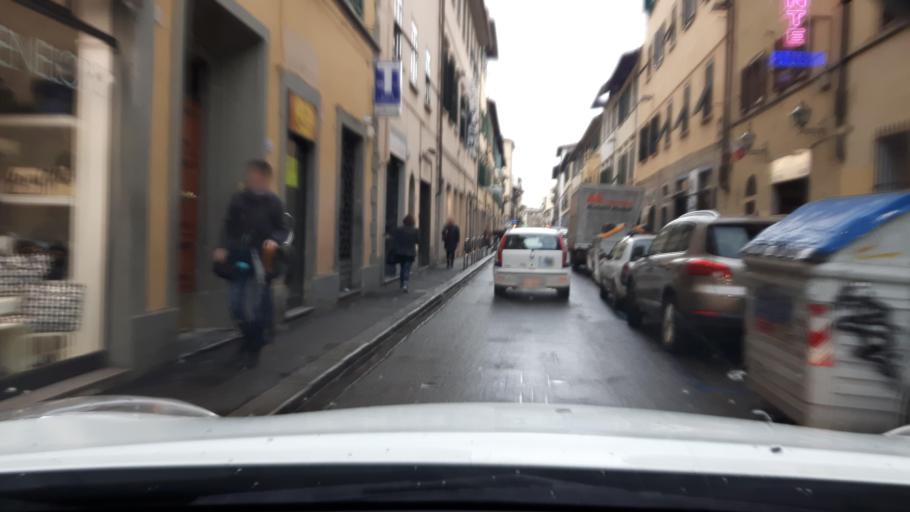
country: IT
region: Tuscany
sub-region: Province of Florence
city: Florence
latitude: 43.7702
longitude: 11.2769
